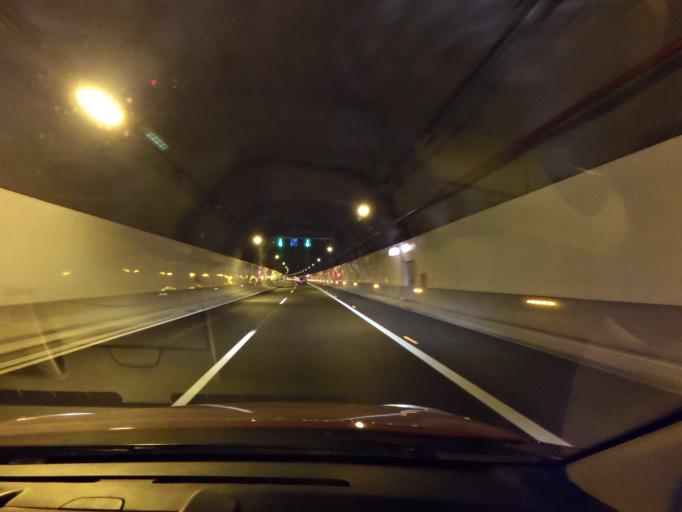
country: ES
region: Canary Islands
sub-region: Provincia de Las Palmas
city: Puerto Rico
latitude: 27.8087
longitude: -15.7222
